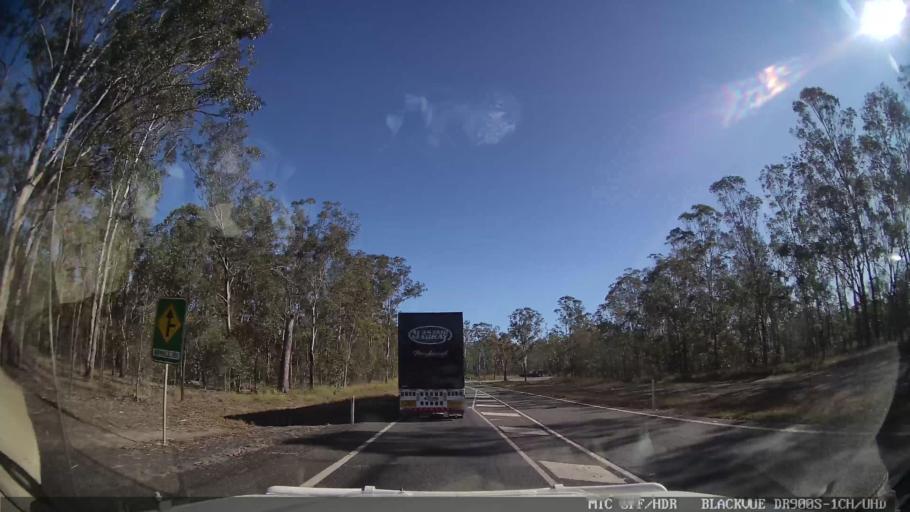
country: AU
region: Queensland
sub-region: Bundaberg
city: Childers
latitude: -25.2110
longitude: 152.0843
